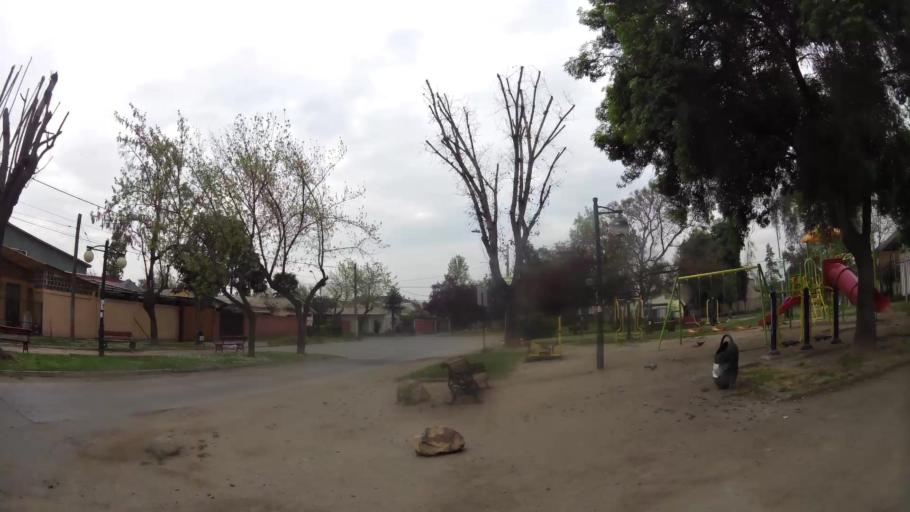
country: CL
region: Santiago Metropolitan
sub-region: Provincia de Santiago
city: Villa Presidente Frei, Nunoa, Santiago, Chile
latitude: -33.4693
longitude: -70.5877
